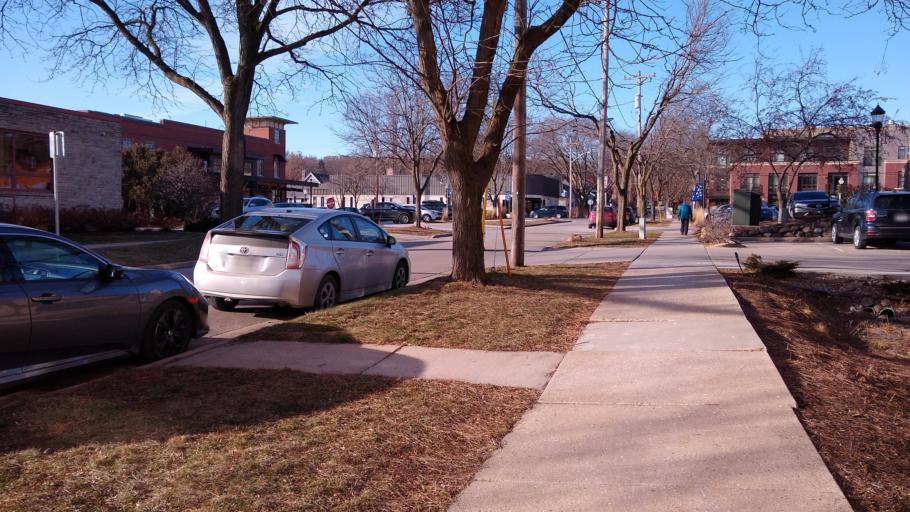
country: US
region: Wisconsin
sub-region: Dane County
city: Shorewood Hills
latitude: 43.0567
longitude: -89.4279
